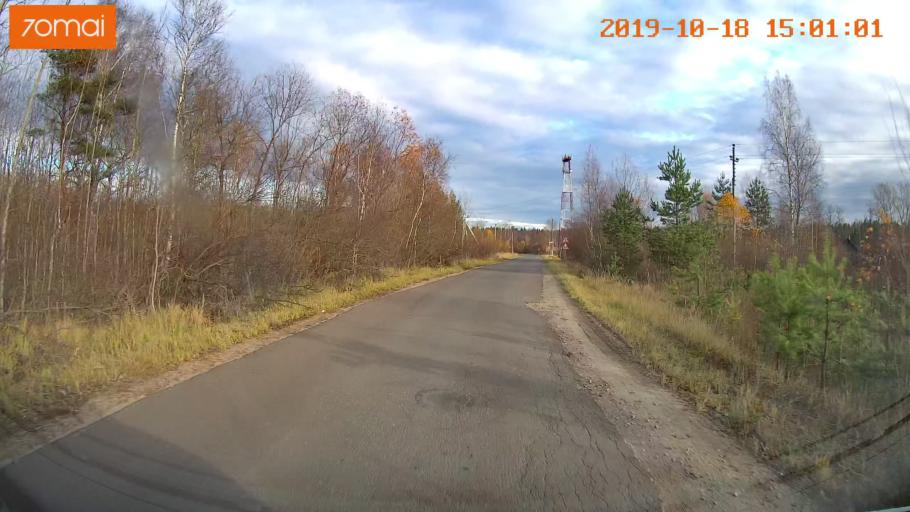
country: RU
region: Vladimir
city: Gus'-Khrustal'nyy
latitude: 55.4999
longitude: 40.5940
